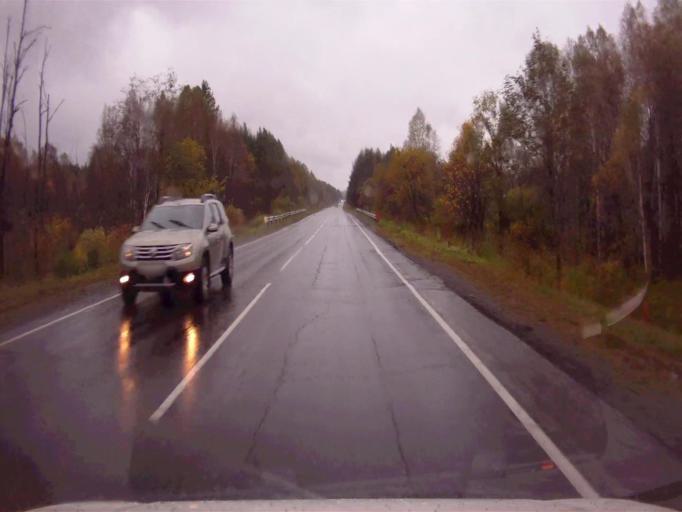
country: RU
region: Chelyabinsk
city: Verkhniy Ufaley
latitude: 55.9729
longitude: 60.3552
